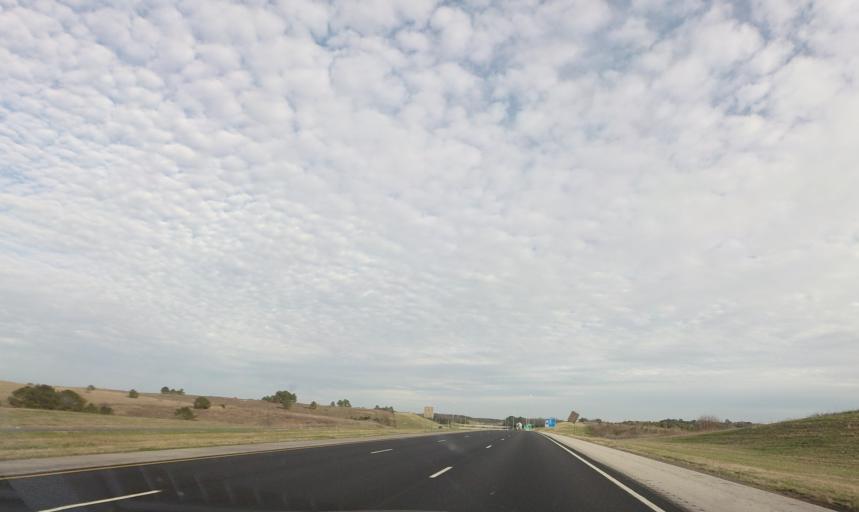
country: US
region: Alabama
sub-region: Jefferson County
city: Graysville
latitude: 33.6465
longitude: -86.9880
